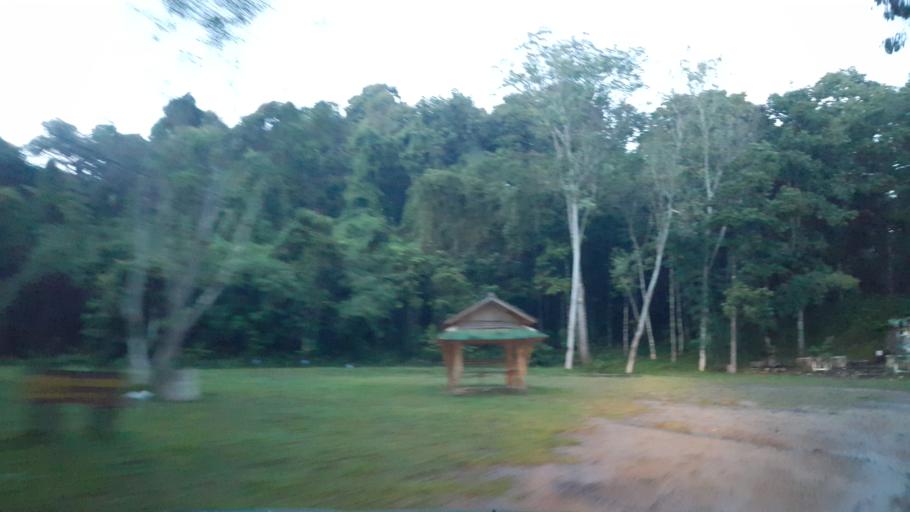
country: TH
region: Chiang Mai
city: Mae On
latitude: 18.7351
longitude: 99.3096
